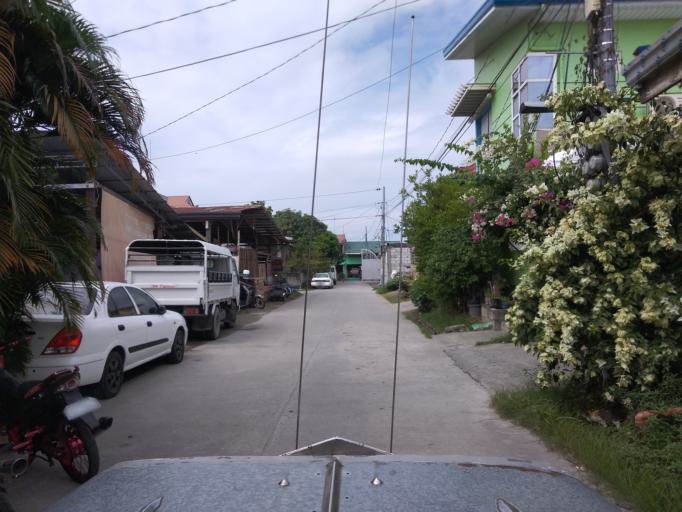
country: PH
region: Central Luzon
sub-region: Province of Pampanga
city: Sexmoan
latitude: 14.9443
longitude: 120.6220
